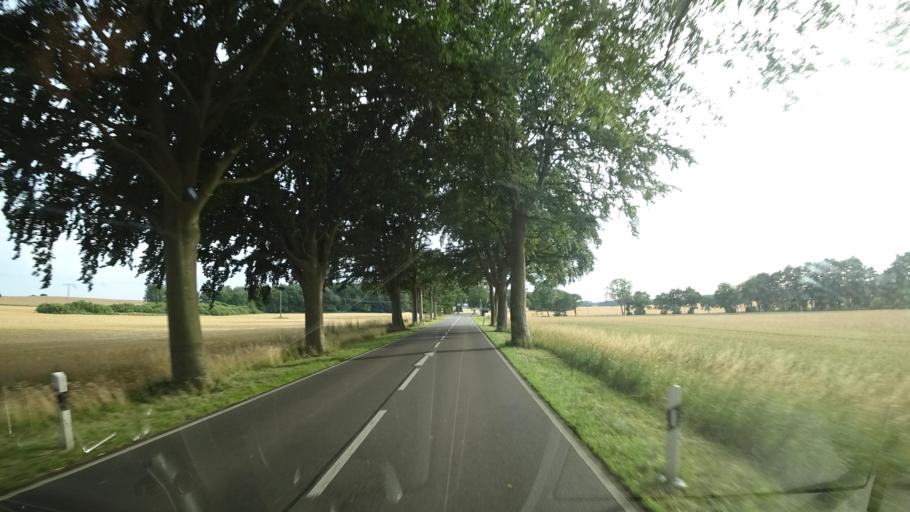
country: DE
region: Mecklenburg-Vorpommern
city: Ostseebad Binz
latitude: 54.4139
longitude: 13.5333
